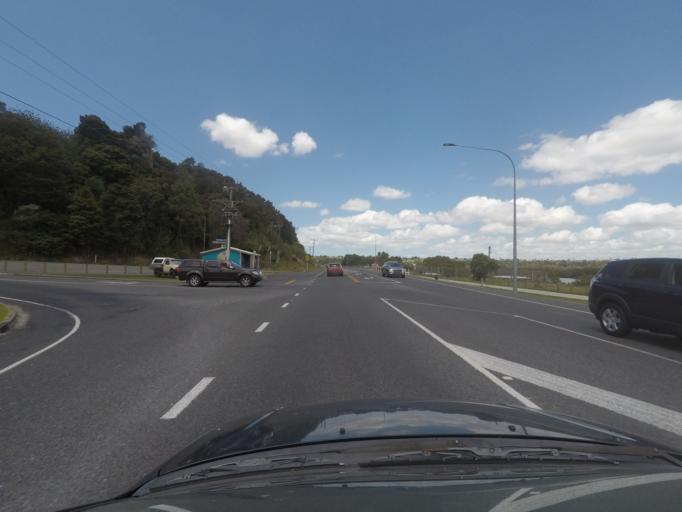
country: NZ
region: Northland
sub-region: Whangarei
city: Whangarei
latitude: -35.7356
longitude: 174.3513
